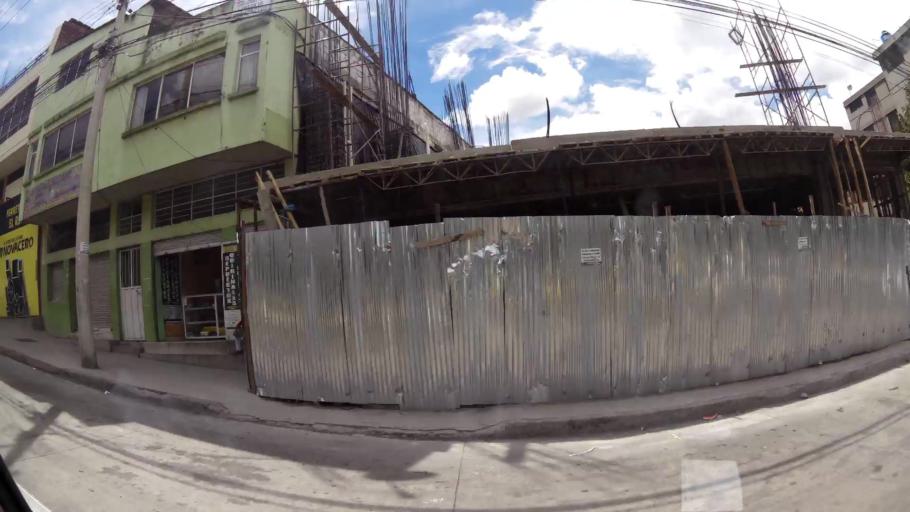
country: EC
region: Tungurahua
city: Ambato
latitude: -1.2387
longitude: -78.6202
